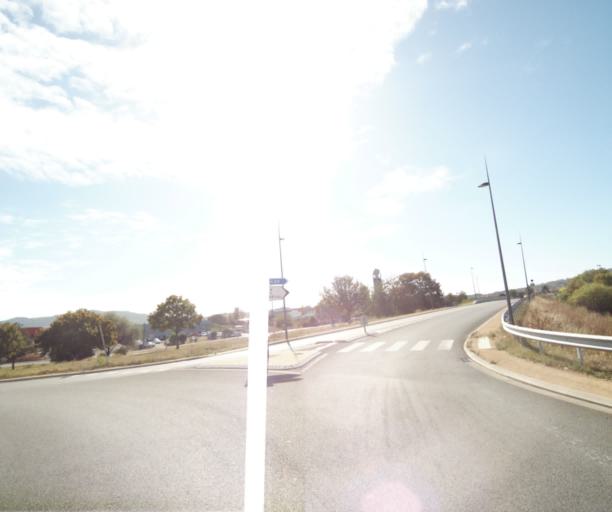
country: FR
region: Auvergne
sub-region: Departement du Puy-de-Dome
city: Malintrat
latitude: 45.7800
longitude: 3.2024
